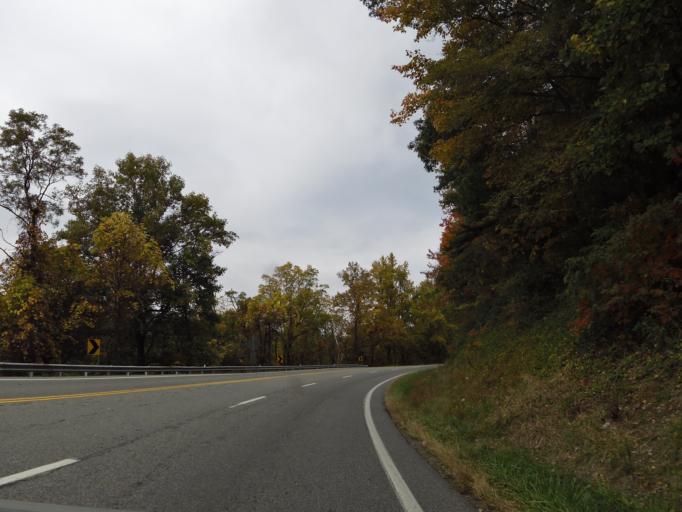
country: US
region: Virginia
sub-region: Carroll County
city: Cana
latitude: 36.6270
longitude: -80.6929
